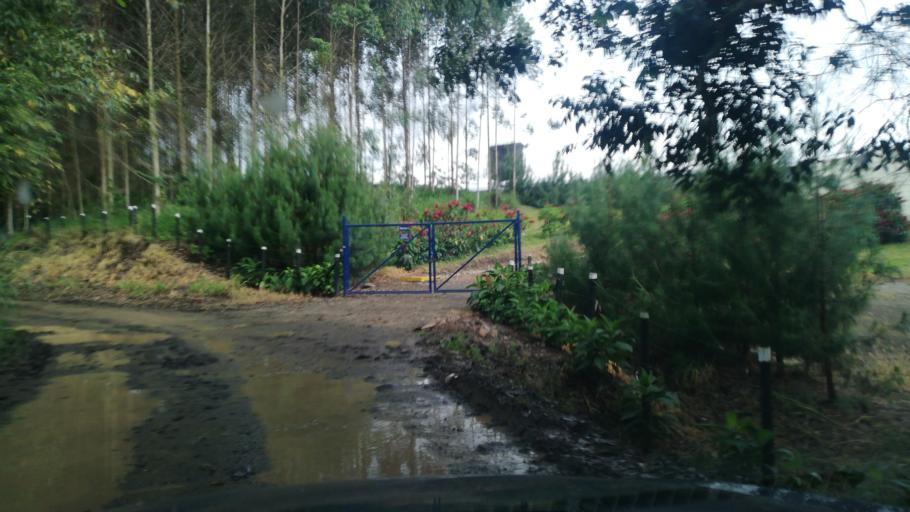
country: CO
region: Valle del Cauca
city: Restrepo
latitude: 3.8537
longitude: -76.4608
